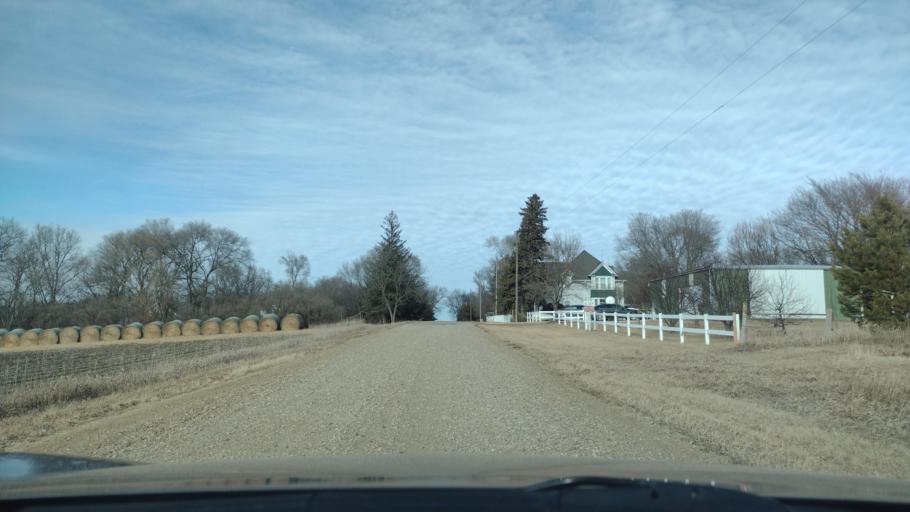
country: US
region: South Dakota
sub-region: Union County
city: Beresford
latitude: 42.9601
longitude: -96.8055
